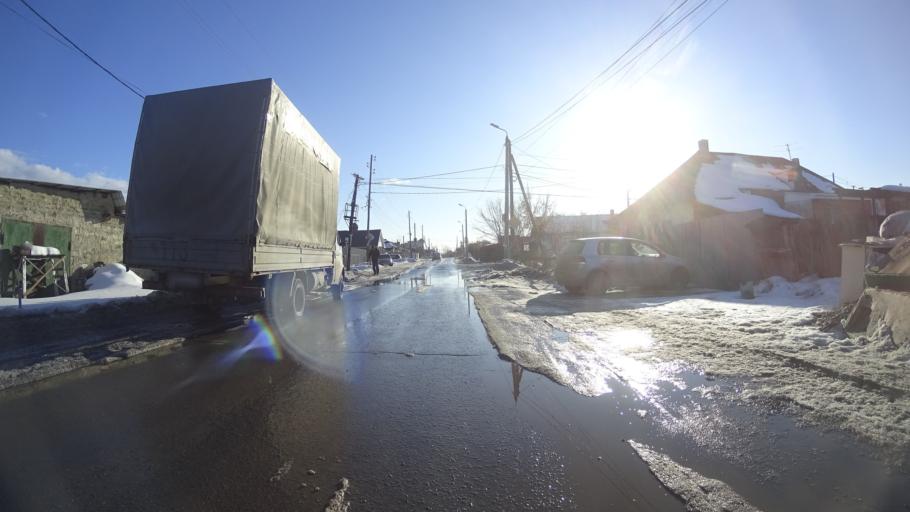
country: RU
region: Chelyabinsk
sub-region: Gorod Chelyabinsk
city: Chelyabinsk
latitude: 55.1524
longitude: 61.3096
